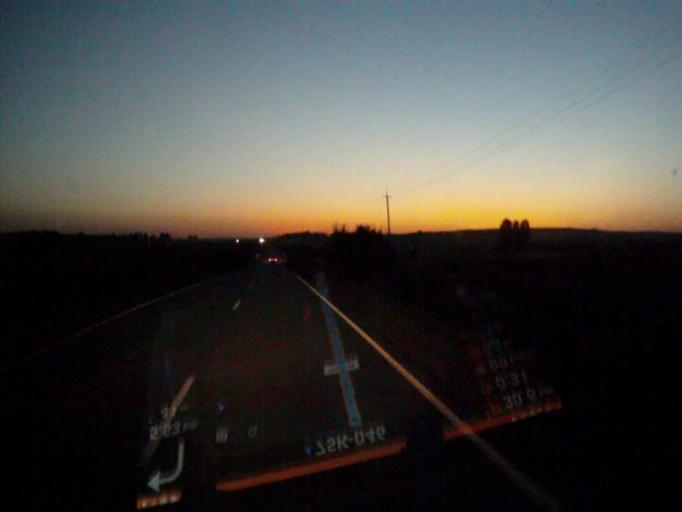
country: RU
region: Chelyabinsk
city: Chebarkul'
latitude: 55.2204
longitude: 60.5348
